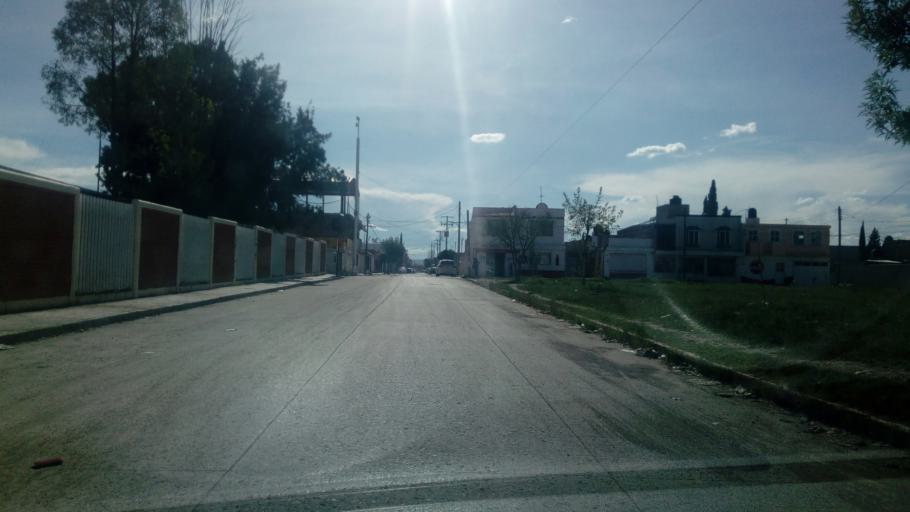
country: MX
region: Durango
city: Victoria de Durango
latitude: 24.0087
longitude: -104.6278
